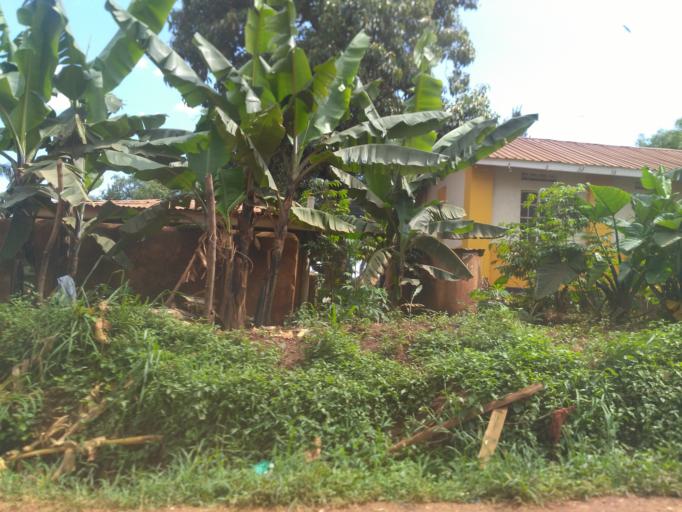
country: UG
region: Central Region
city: Kampala Central Division
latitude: 0.3430
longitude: 32.5694
